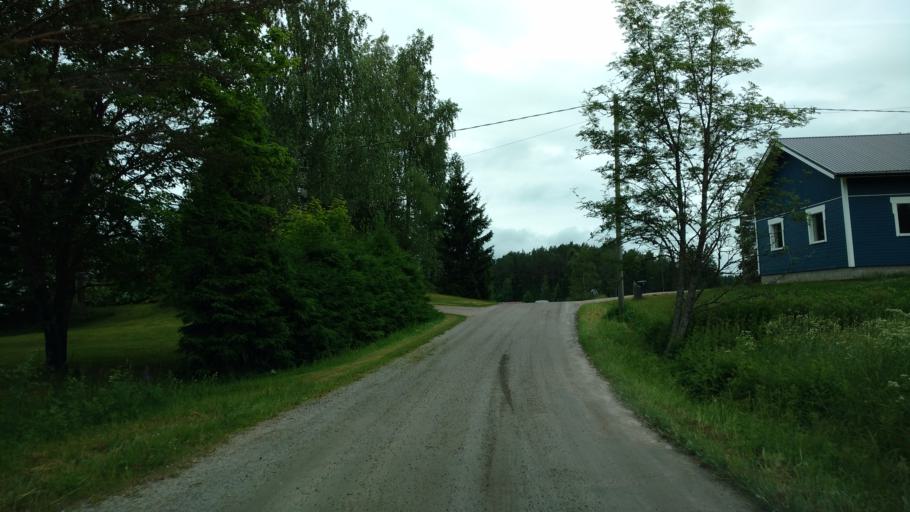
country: FI
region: Varsinais-Suomi
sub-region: Salo
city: Halikko
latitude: 60.4666
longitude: 22.9810
